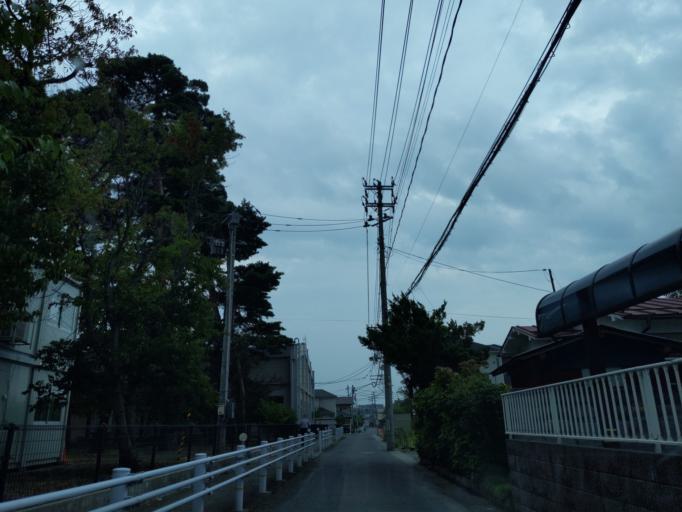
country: JP
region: Fukushima
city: Koriyama
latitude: 37.3914
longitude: 140.3486
